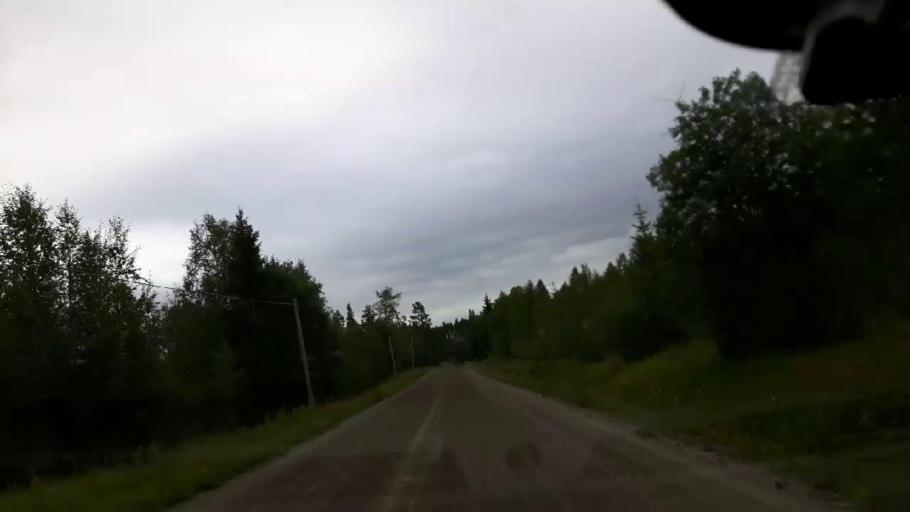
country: SE
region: Jaemtland
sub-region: Braecke Kommun
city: Braecke
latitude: 62.8953
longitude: 15.6033
